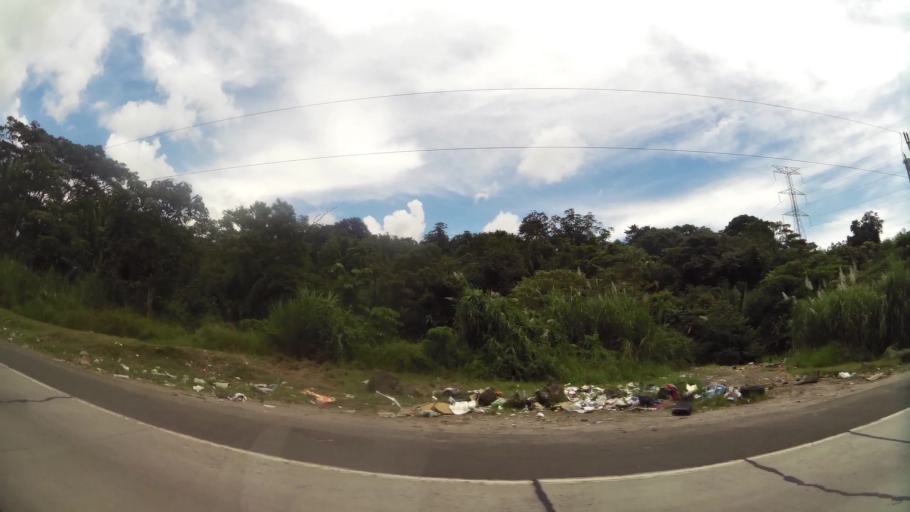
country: PA
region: Panama
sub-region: Distrito Arraijan
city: Arraijan
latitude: 8.9749
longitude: -79.6442
